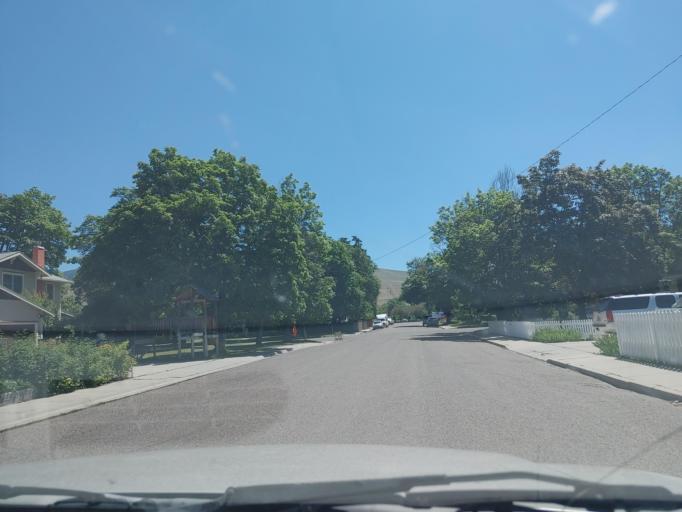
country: US
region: Montana
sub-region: Missoula County
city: Missoula
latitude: 46.8620
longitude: -114.0086
